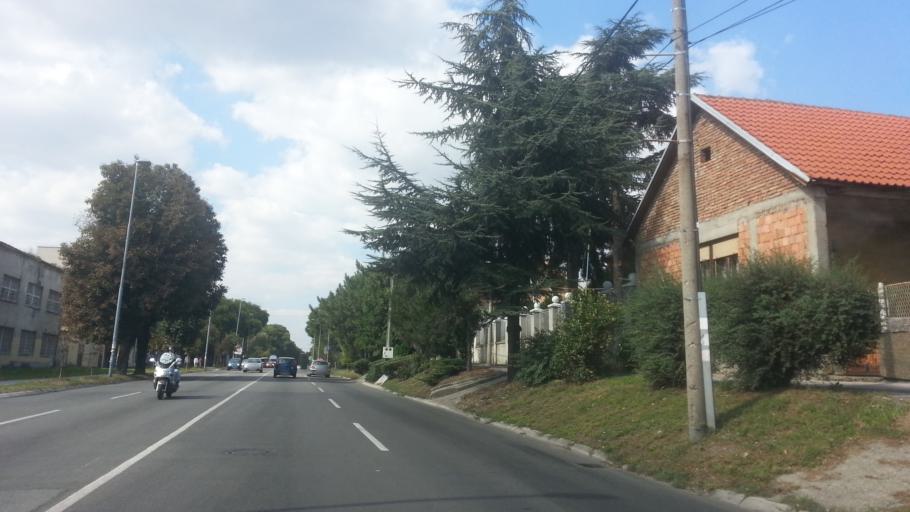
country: RS
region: Central Serbia
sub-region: Belgrade
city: Zemun
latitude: 44.8538
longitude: 20.3904
